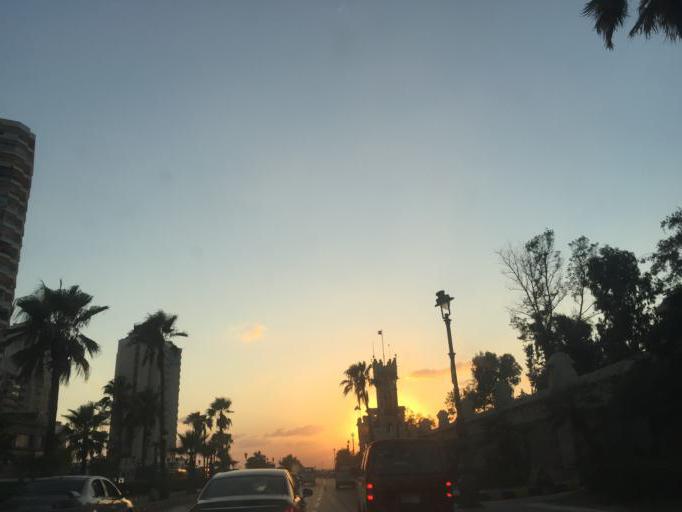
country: EG
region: Alexandria
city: Alexandria
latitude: 31.2811
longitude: 30.0147
